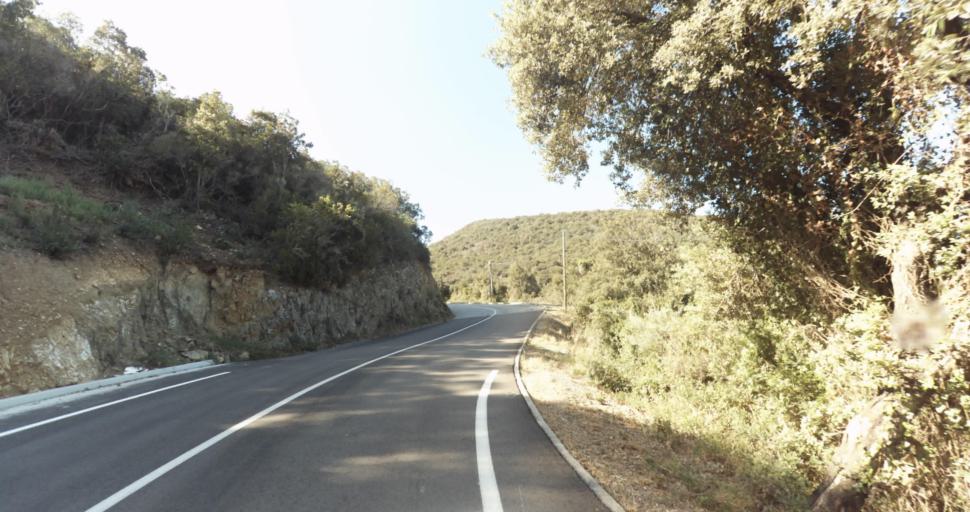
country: FR
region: Corsica
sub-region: Departement de la Corse-du-Sud
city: Ajaccio
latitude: 41.9243
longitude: 8.6431
